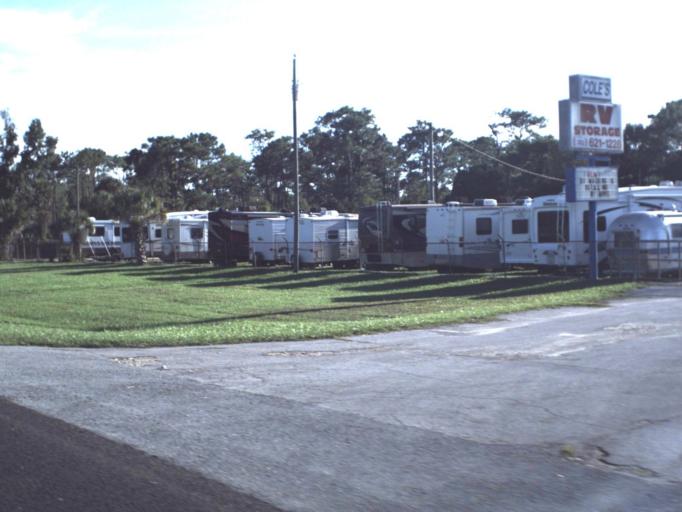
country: US
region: Florida
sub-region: Citrus County
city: Sugarmill Woods
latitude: 28.7541
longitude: -82.5531
